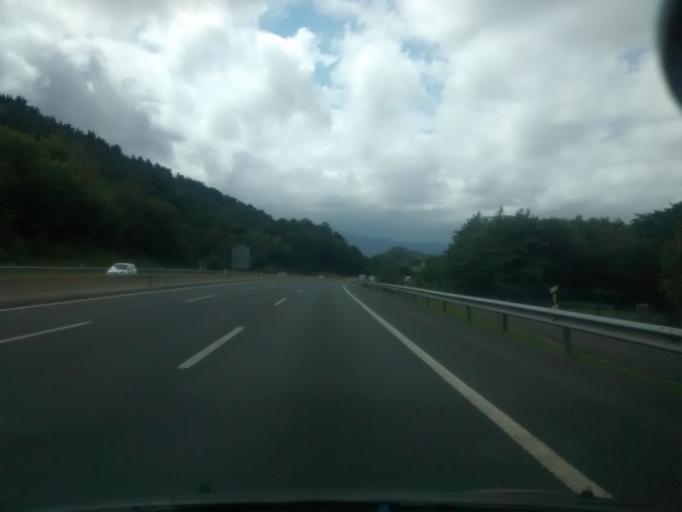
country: ES
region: Basque Country
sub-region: Provincia de Guipuzcoa
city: Usurbil
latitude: 43.2937
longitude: -2.0647
